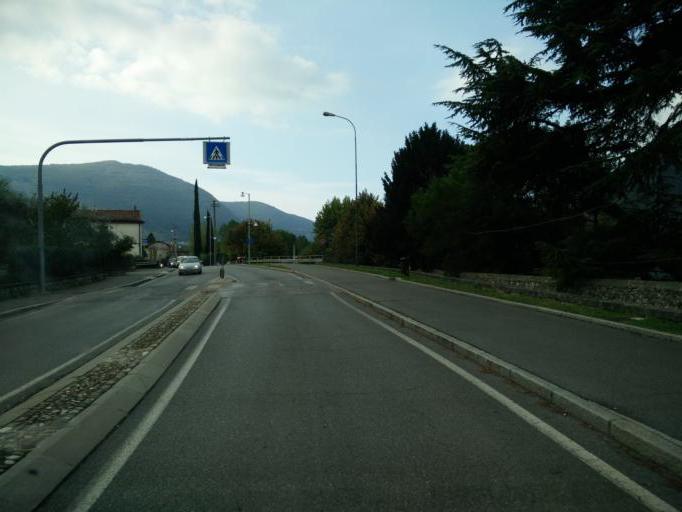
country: IT
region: Lombardy
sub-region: Provincia di Brescia
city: Sale Marasino
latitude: 45.7056
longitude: 10.1086
